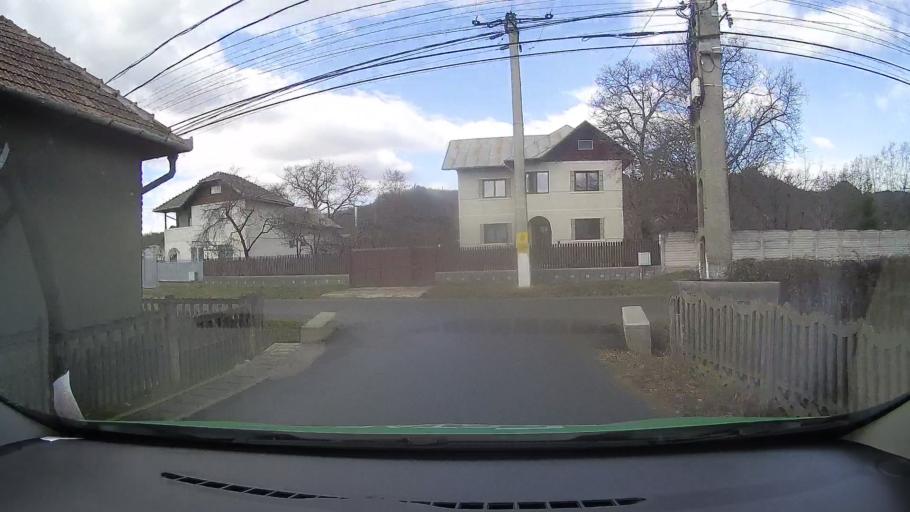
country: RO
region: Dambovita
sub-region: Comuna Buciumeni
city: Buciumeni
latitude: 45.1527
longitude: 25.4518
